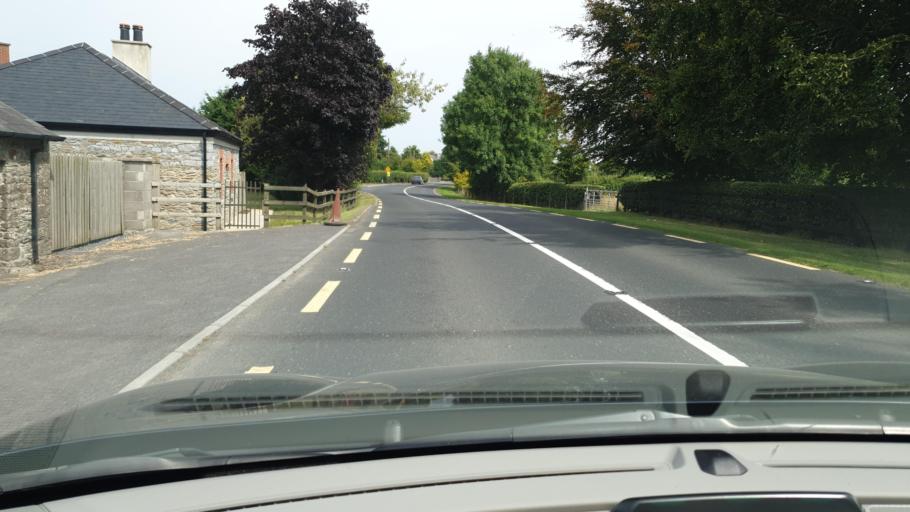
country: IE
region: Leinster
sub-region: An Mhi
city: Kells
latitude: 53.7097
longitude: -6.9087
